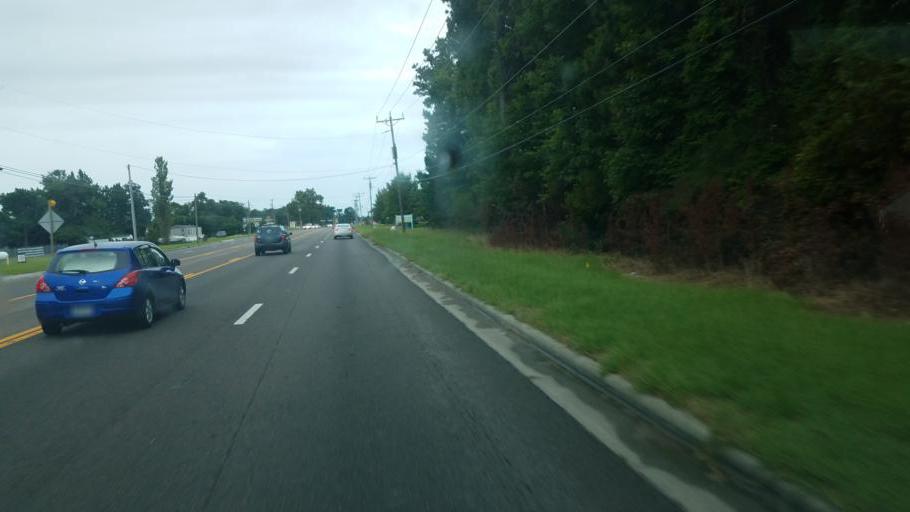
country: US
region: North Carolina
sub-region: Dare County
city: Southern Shores
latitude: 36.2376
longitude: -75.8750
